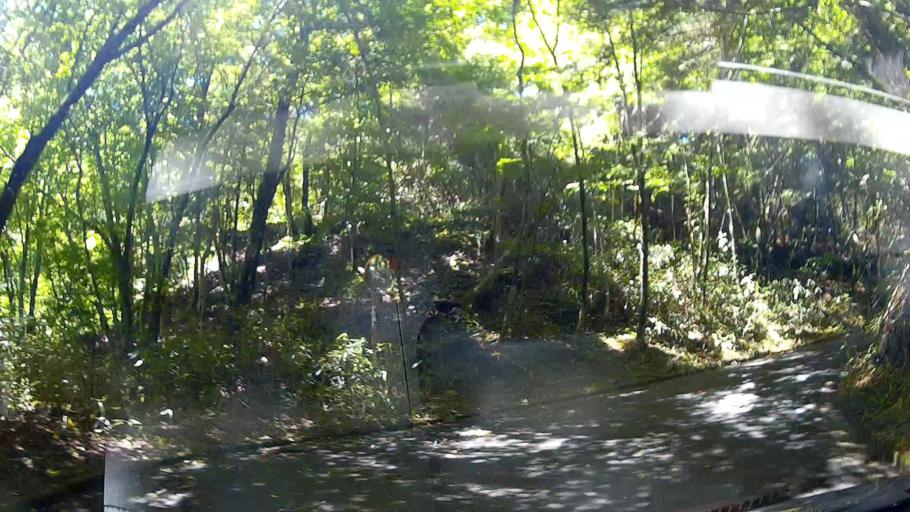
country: JP
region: Shizuoka
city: Fujinomiya
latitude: 35.2827
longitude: 138.3213
